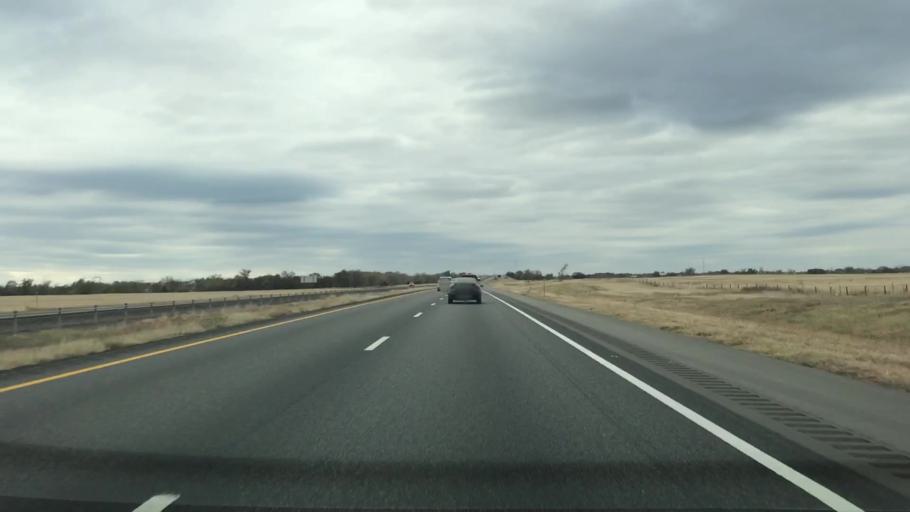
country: US
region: Oklahoma
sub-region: Beckham County
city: Elk City
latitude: 35.3858
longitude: -99.4388
